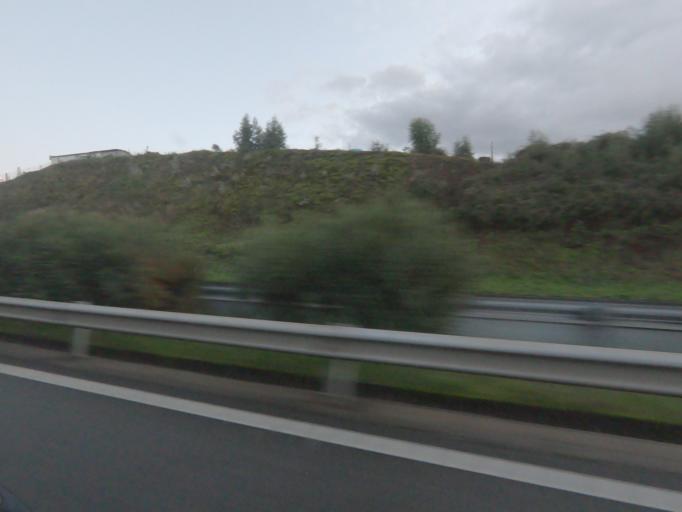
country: PT
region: Porto
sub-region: Penafiel
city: Penafiel
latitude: 41.2198
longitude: -8.2609
